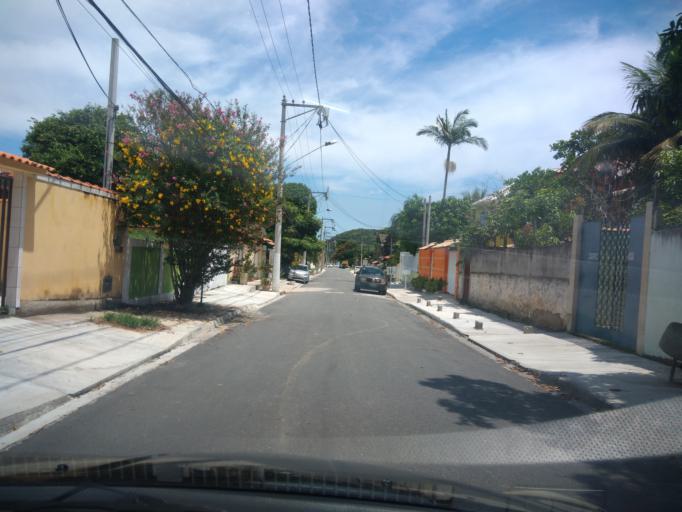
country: BR
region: Rio de Janeiro
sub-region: Niteroi
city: Niteroi
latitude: -22.9284
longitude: -43.0703
